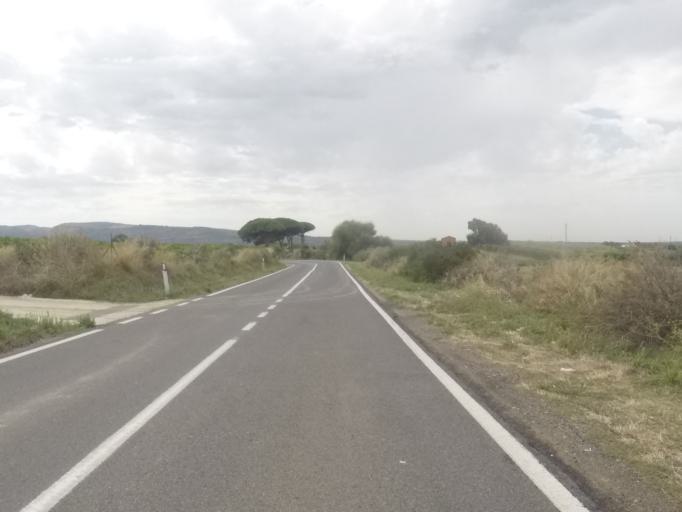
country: IT
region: Sardinia
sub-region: Provincia di Sassari
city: Sorso
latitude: 40.8409
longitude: 8.6035
